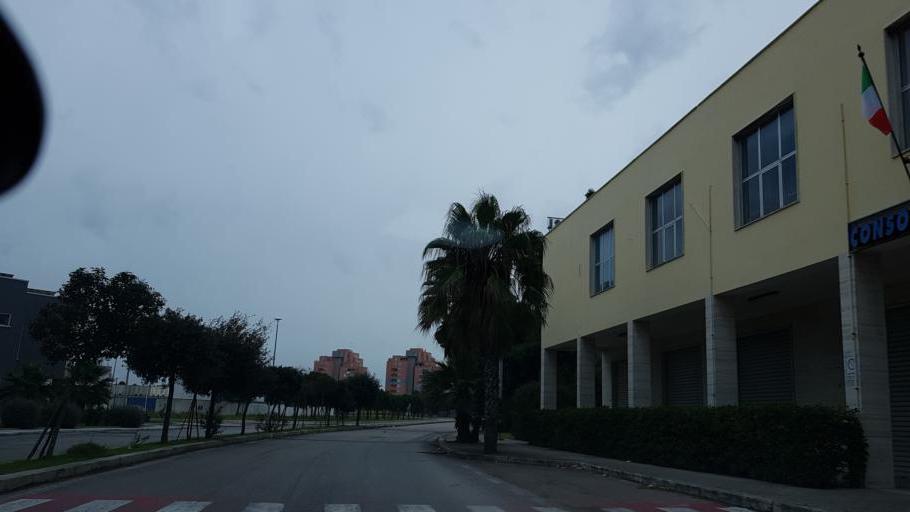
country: IT
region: Apulia
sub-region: Provincia di Brindisi
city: Brindisi
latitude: 40.6359
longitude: 17.9544
